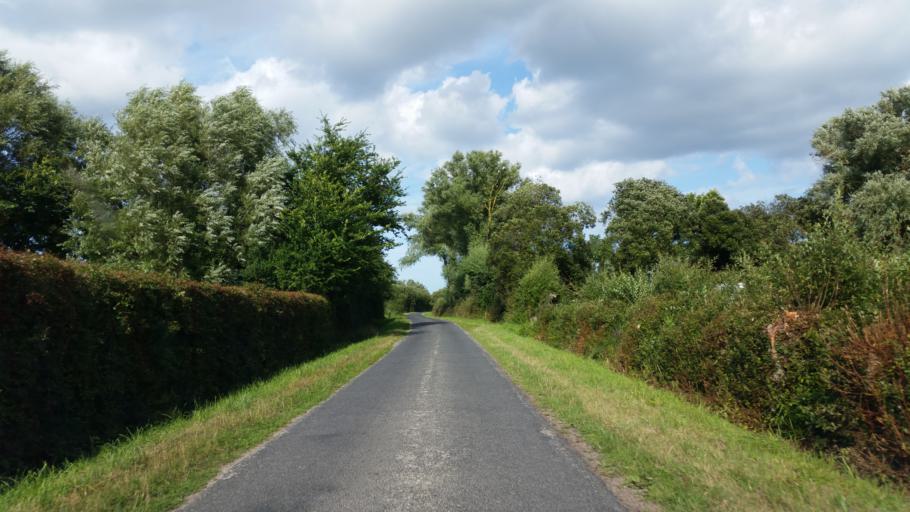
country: FR
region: Lower Normandy
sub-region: Departement de la Manche
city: Sainte-Mere-Eglise
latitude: 49.4511
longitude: -1.2502
